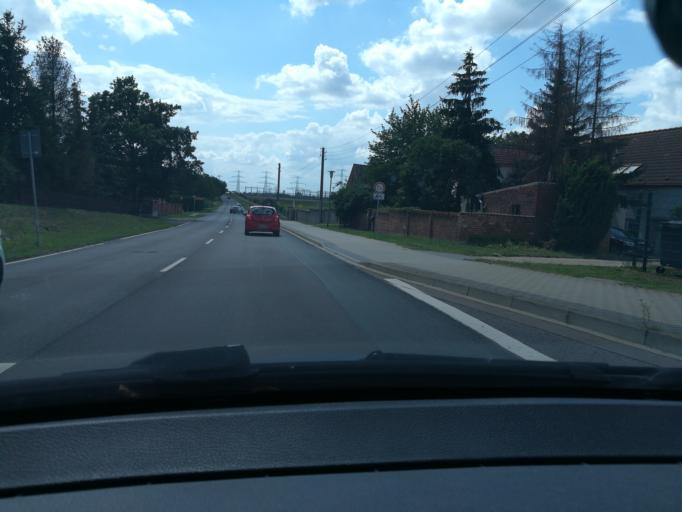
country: DE
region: Saxony-Anhalt
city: Zielitz
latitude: 52.2765
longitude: 11.6514
